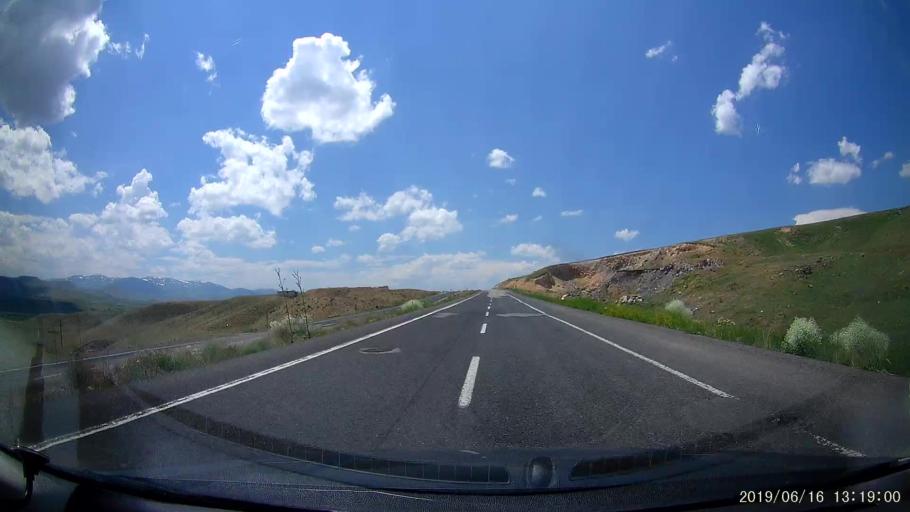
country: TR
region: Agri
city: Taslicay
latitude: 39.6323
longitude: 43.4182
